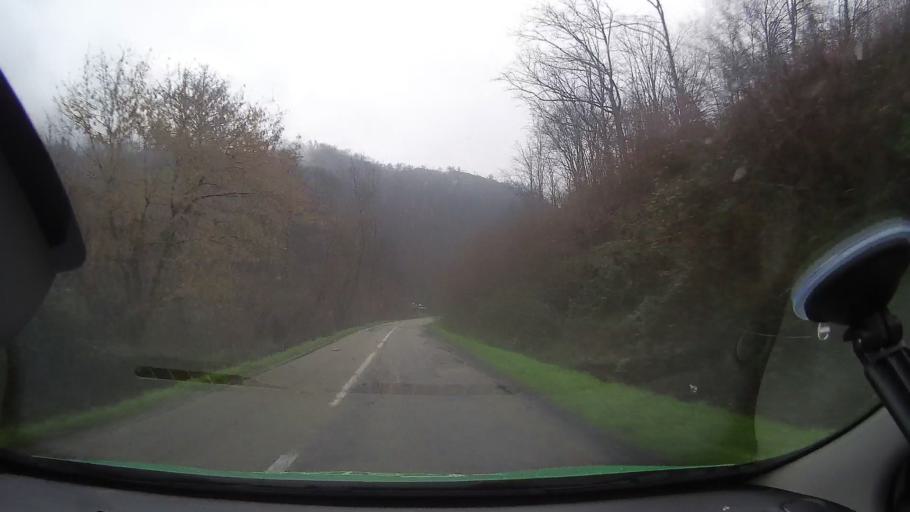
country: RO
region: Arad
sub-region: Comuna Dezna
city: Dezna
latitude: 46.4059
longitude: 22.2547
